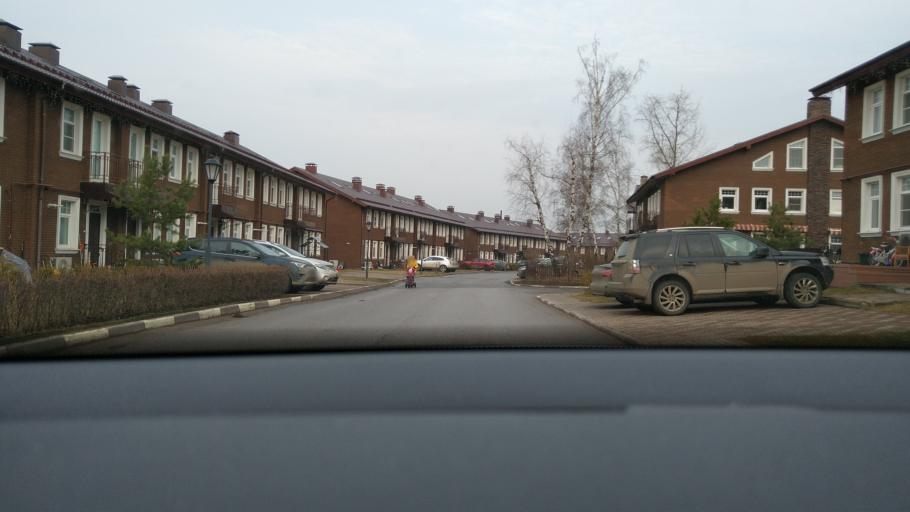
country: RU
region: Moskovskaya
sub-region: Leninskiy Rayon
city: Vnukovo
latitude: 55.6124
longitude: 37.3243
